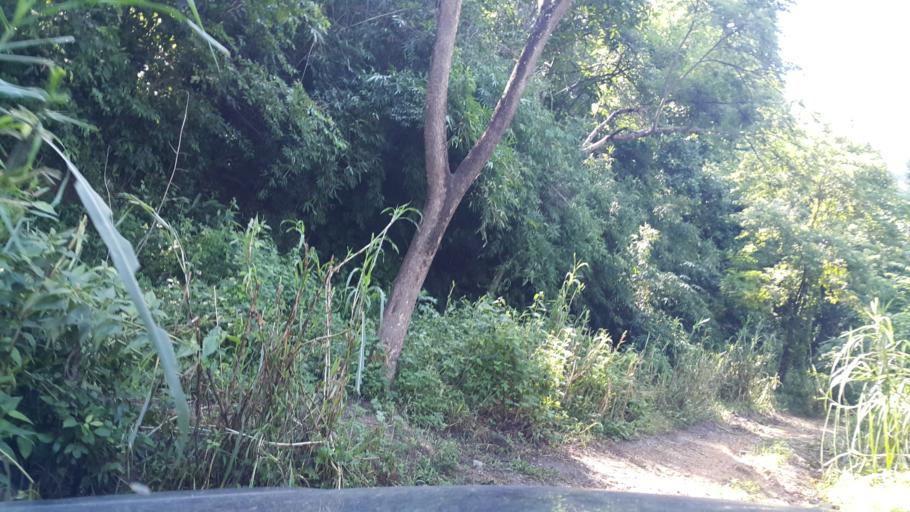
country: TH
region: Chiang Mai
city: San Sai
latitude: 18.9559
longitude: 99.1389
